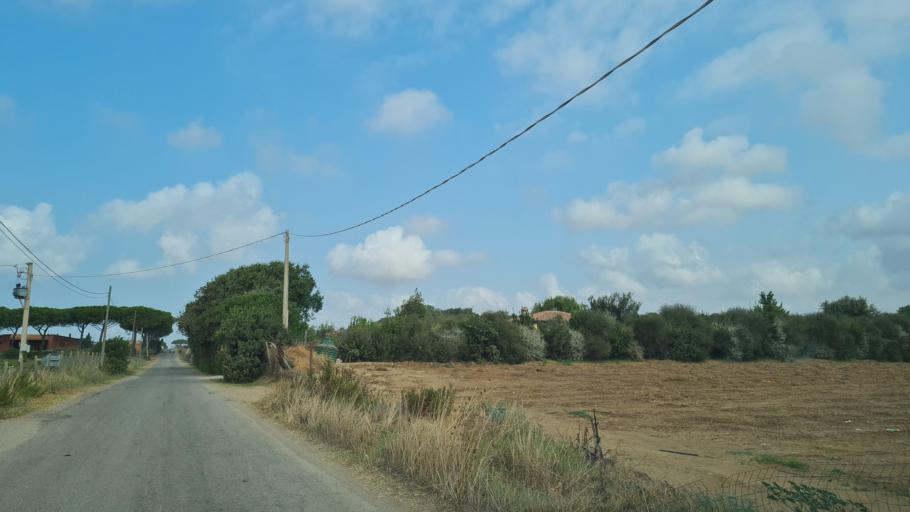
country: IT
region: Latium
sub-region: Provincia di Viterbo
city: Montalto di Castro
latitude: 42.3087
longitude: 11.6213
